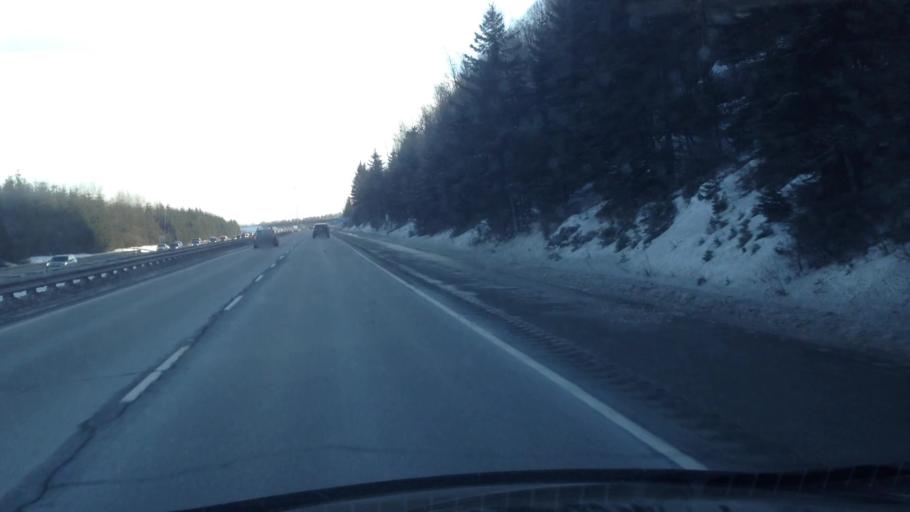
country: CA
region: Quebec
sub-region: Laurentides
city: Prevost
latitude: 45.8498
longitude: -74.0741
